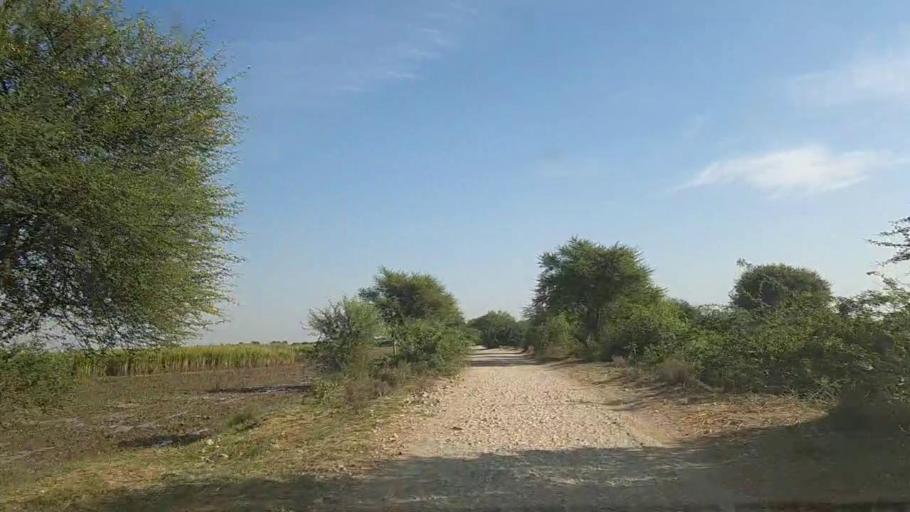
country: PK
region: Sindh
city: Bulri
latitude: 24.8006
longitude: 68.3354
